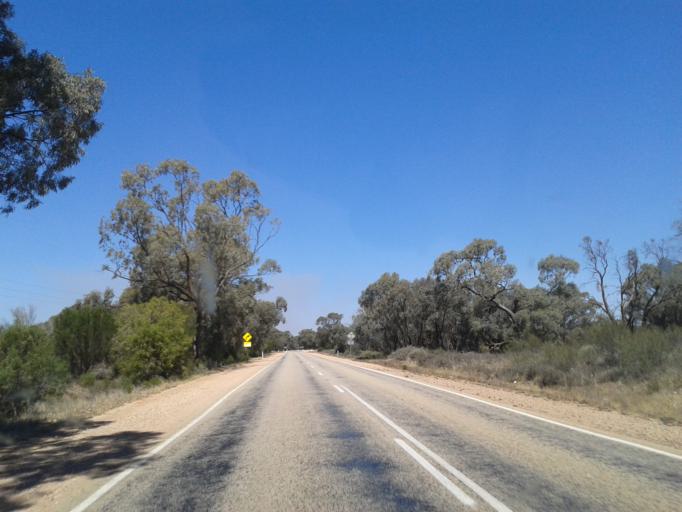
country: AU
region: Victoria
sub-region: Swan Hill
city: Swan Hill
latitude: -34.8230
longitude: 143.2633
